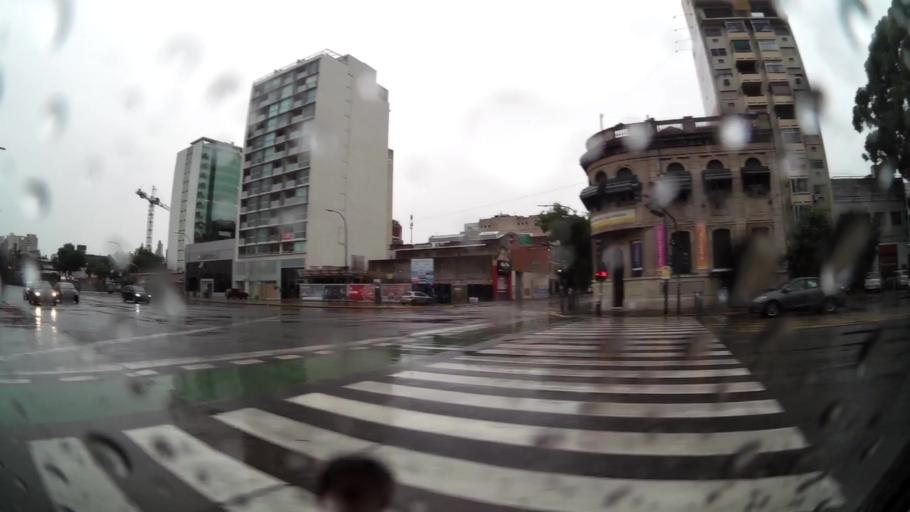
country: AR
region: Buenos Aires F.D.
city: Buenos Aires
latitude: -34.6255
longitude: -58.3680
